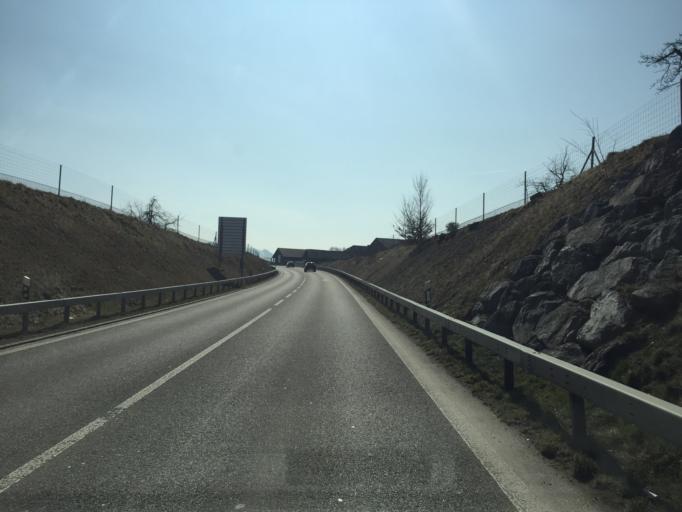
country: CH
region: Saint Gallen
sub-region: Wahlkreis Toggenburg
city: Lutisburg
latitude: 47.4045
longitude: 9.0692
